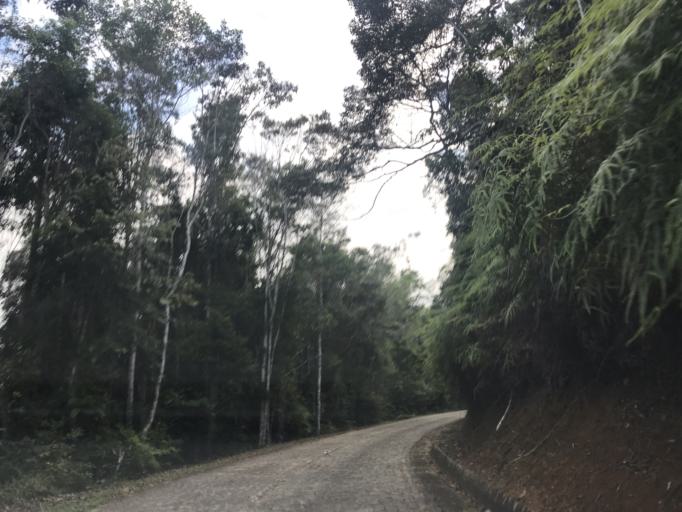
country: BR
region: Bahia
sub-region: Gandu
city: Gandu
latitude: -13.9106
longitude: -39.4612
